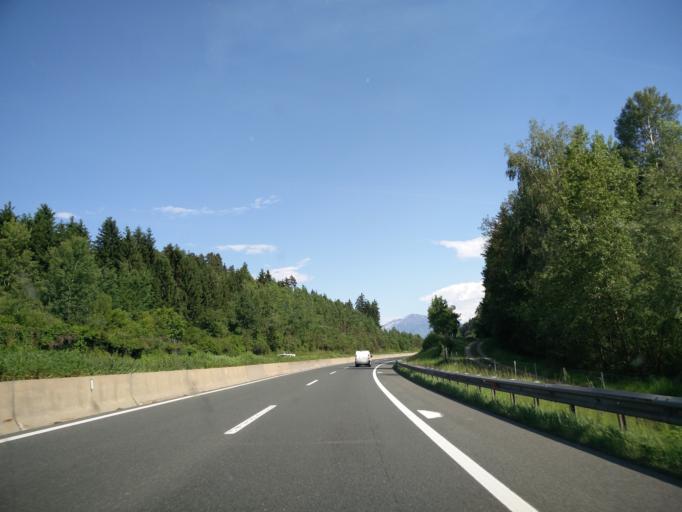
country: AT
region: Carinthia
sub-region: Politischer Bezirk Klagenfurt Land
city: Poggersdorf
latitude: 46.6531
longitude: 14.5365
